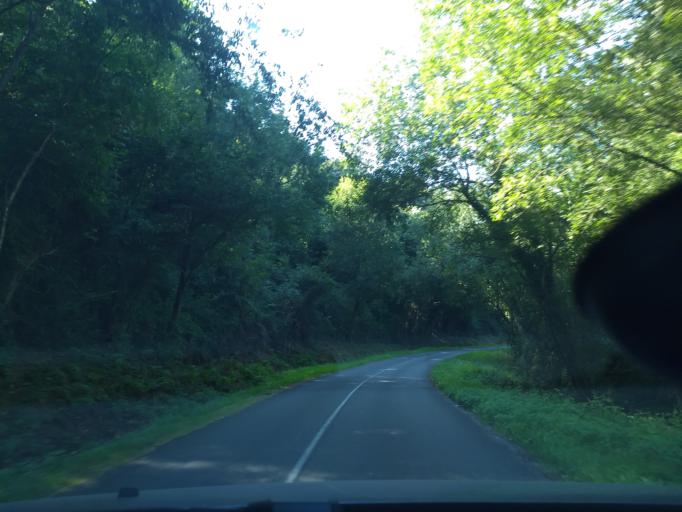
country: FR
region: Aquitaine
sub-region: Departement des Pyrenees-Atlantiques
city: Soumoulou
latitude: 43.2915
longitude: -0.1493
